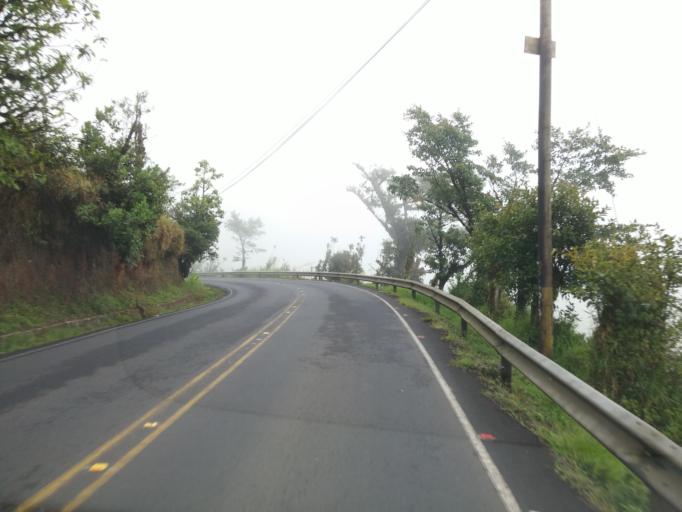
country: CR
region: Alajuela
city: San Ramon
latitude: 10.1598
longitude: -84.4946
